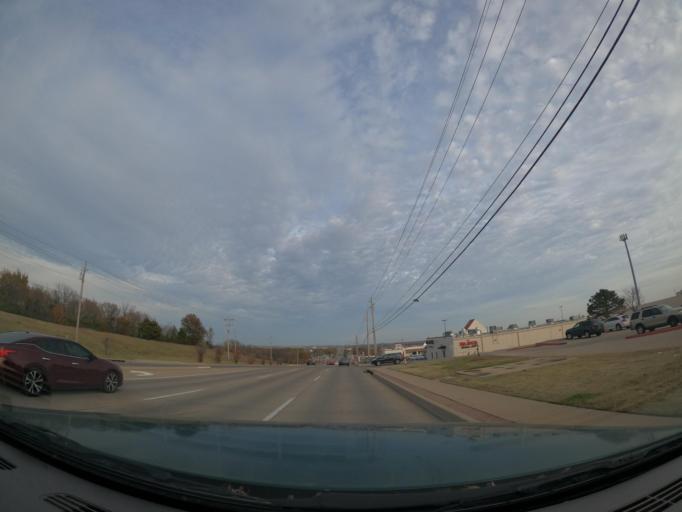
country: US
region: Oklahoma
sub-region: Tulsa County
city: Jenks
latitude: 36.0607
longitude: -95.9086
